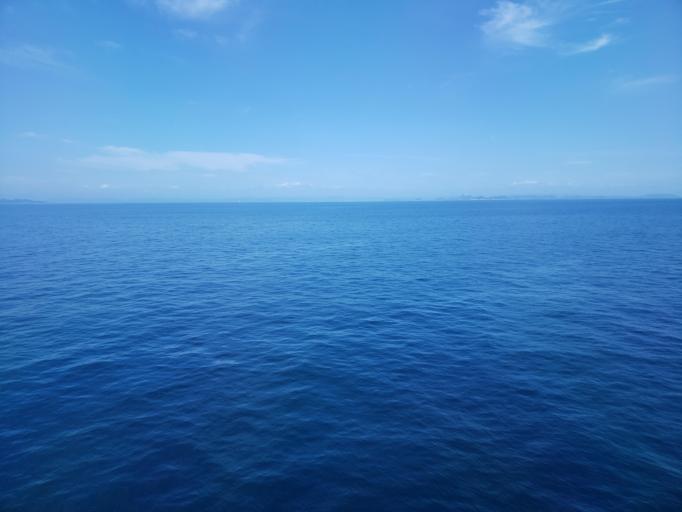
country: JP
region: Tokushima
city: Narutocho-mitsuishi
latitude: 34.4691
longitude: 134.4924
